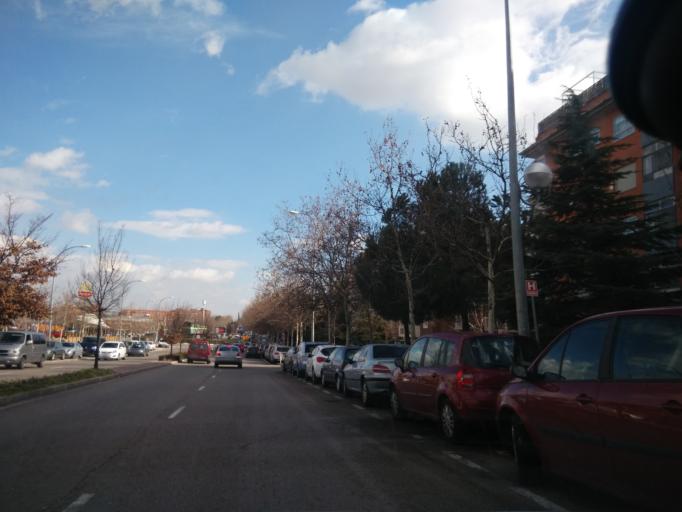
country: ES
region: Madrid
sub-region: Provincia de Madrid
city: Alcobendas
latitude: 40.5475
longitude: -3.6588
